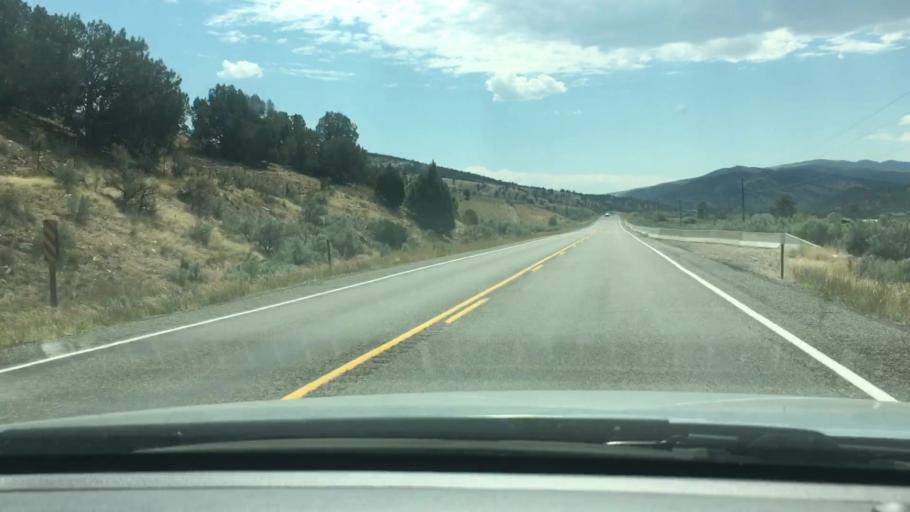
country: US
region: Utah
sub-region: Utah County
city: Woodland Hills
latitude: 39.9122
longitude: -111.5510
